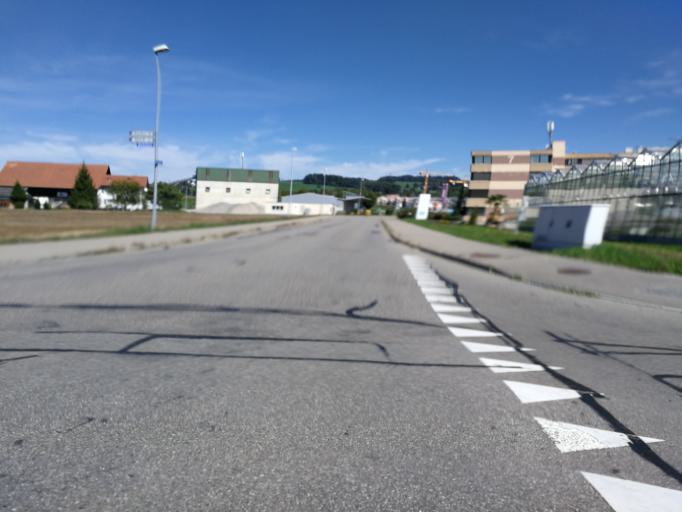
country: CH
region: Zurich
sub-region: Bezirk Pfaeffikon
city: Pfaeffikon / Pfaeffikon (Dorfkern)
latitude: 47.3704
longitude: 8.7718
